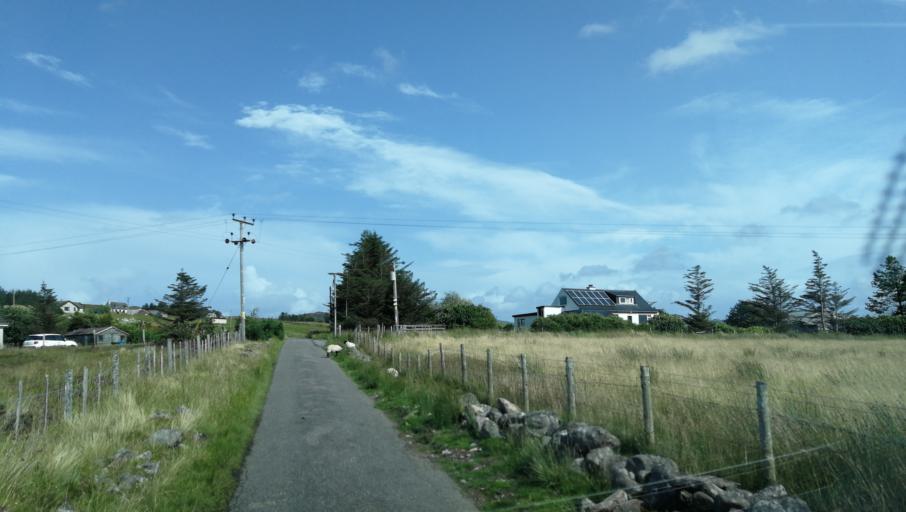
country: GB
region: Scotland
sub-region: Highland
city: Portree
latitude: 57.7450
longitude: -5.7751
